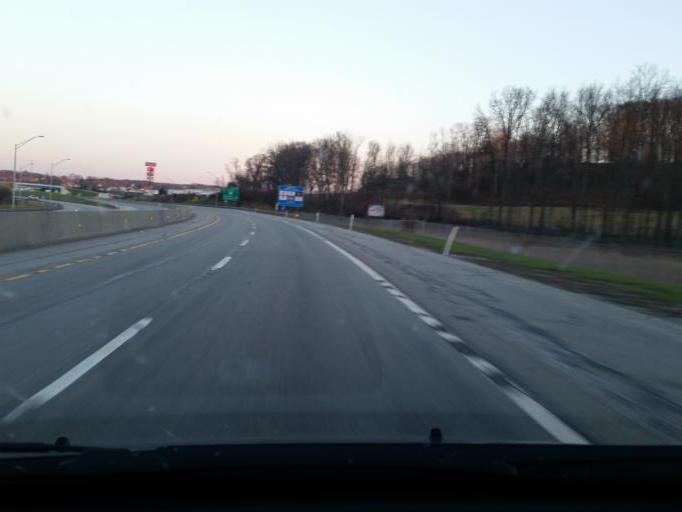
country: US
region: Pennsylvania
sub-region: Somerset County
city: Somerset
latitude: 40.0241
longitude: -79.0889
